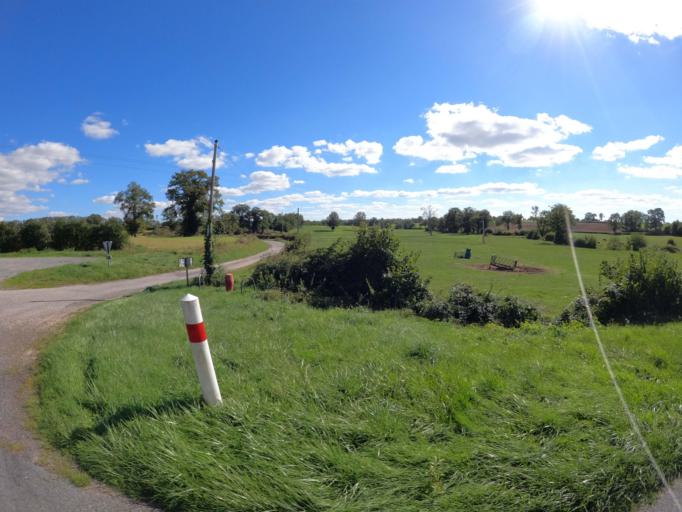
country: FR
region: Auvergne
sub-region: Departement de l'Allier
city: Doyet
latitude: 46.3973
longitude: 2.8367
